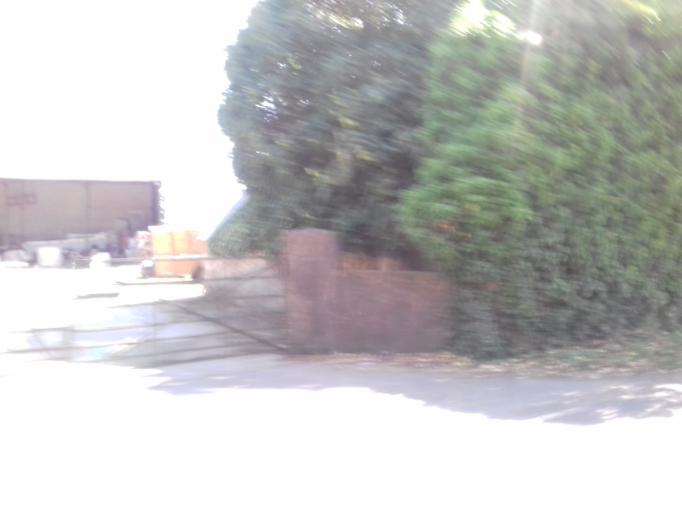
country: IE
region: Leinster
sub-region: Fingal County
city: Swords
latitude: 53.5118
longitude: -6.2679
